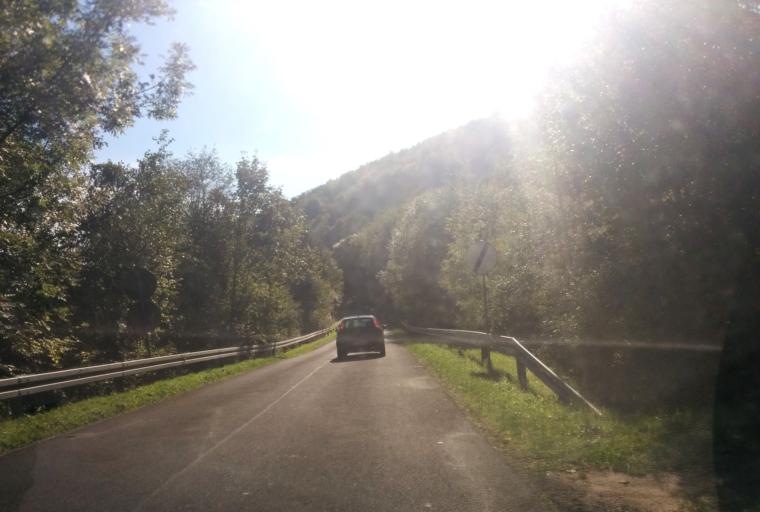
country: PL
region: Subcarpathian Voivodeship
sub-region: Powiat leski
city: Polanczyk
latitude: 49.3265
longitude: 22.4169
